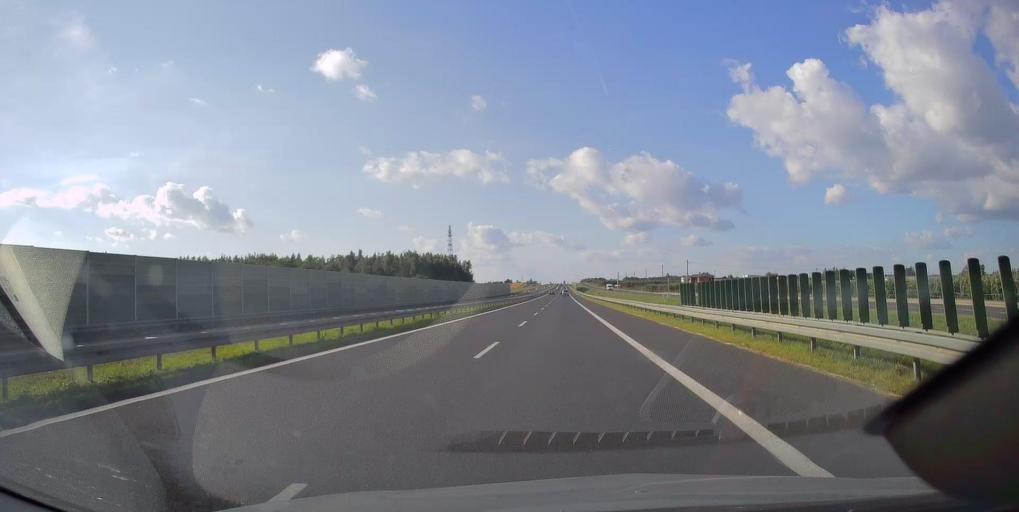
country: PL
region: Masovian Voivodeship
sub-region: Powiat bialobrzeski
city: Promna
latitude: 51.7086
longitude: 20.9263
